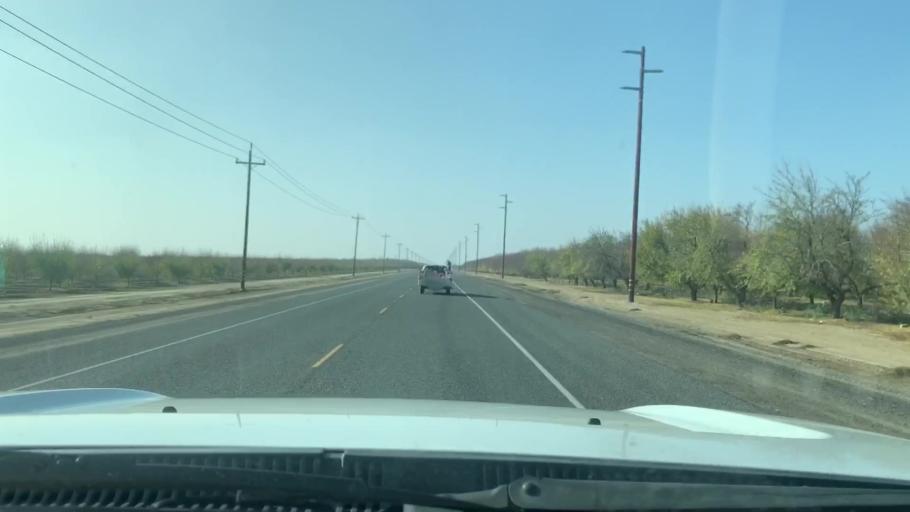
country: US
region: California
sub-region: Kern County
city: Wasco
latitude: 35.6013
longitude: -119.4497
